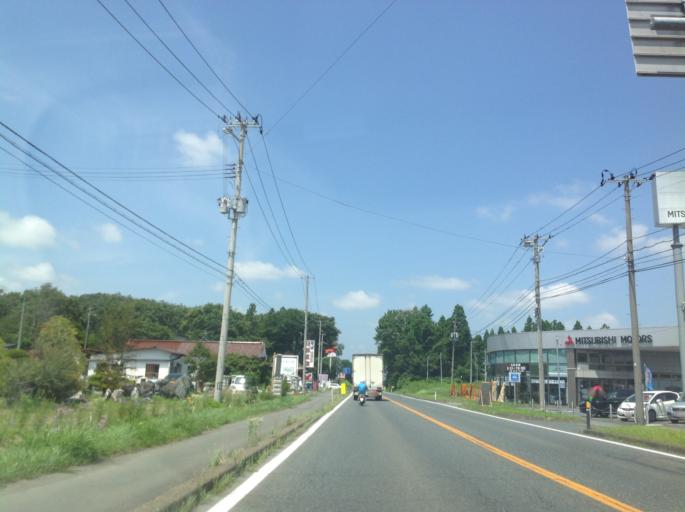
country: JP
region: Iwate
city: Hanamaki
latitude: 39.3393
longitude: 141.1082
